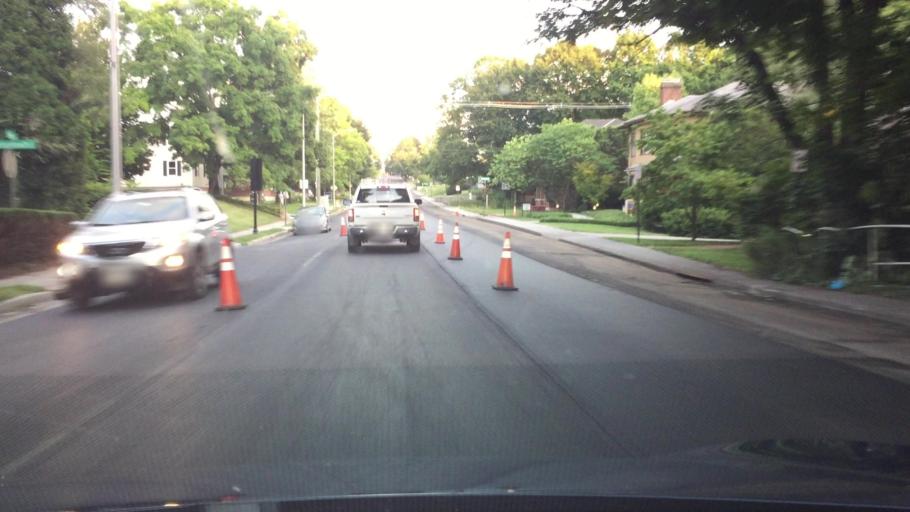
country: US
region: Virginia
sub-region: Montgomery County
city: Blacksburg
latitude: 37.2254
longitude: -80.4097
